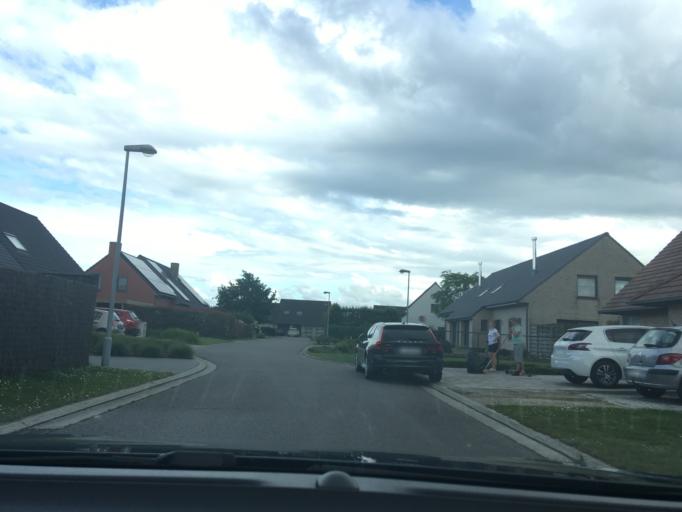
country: BE
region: Flanders
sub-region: Provincie West-Vlaanderen
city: Moorslede
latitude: 50.9374
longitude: 3.0631
